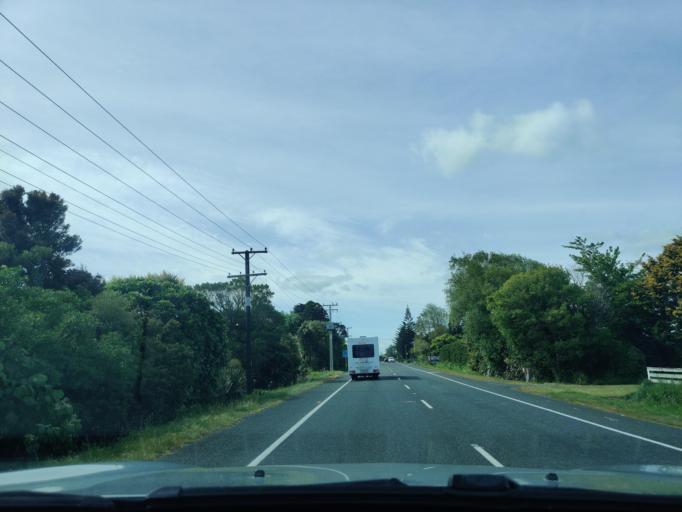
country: NZ
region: Taranaki
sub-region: New Plymouth District
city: New Plymouth
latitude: -39.0903
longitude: 174.1027
